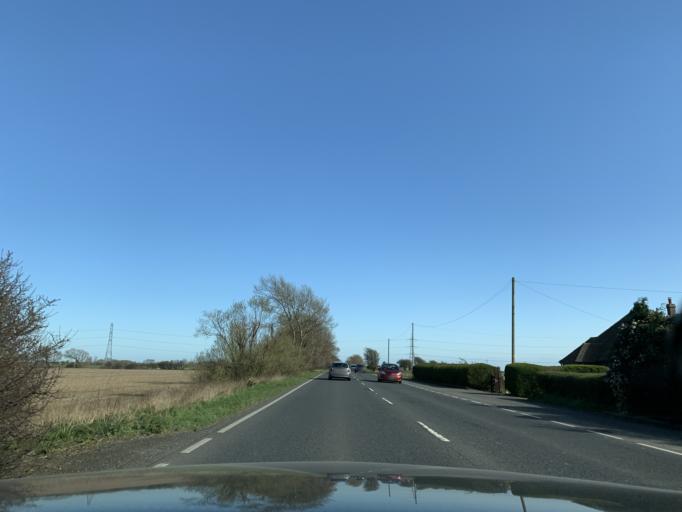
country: GB
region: England
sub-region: Kent
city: Romney Marsh
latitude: 50.9881
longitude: 0.9042
